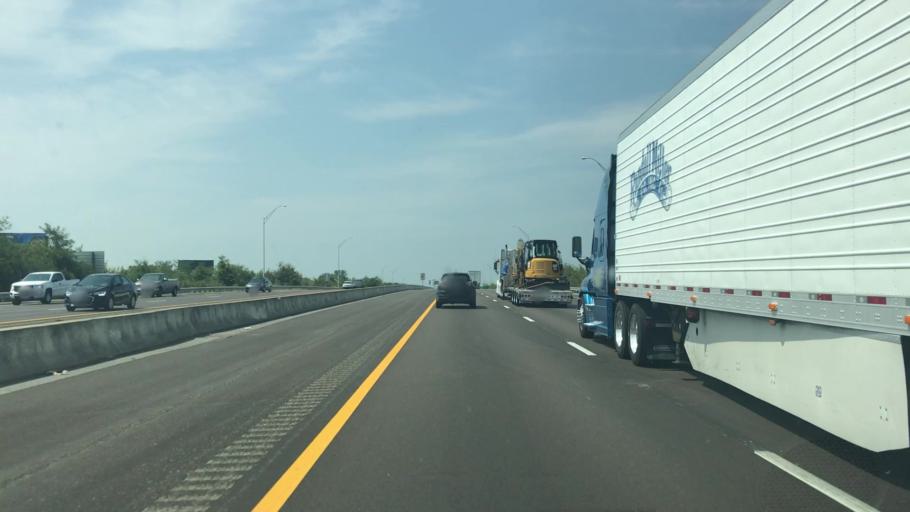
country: US
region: Tennessee
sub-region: Shelby County
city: Bartlett
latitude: 35.1811
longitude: -89.9114
